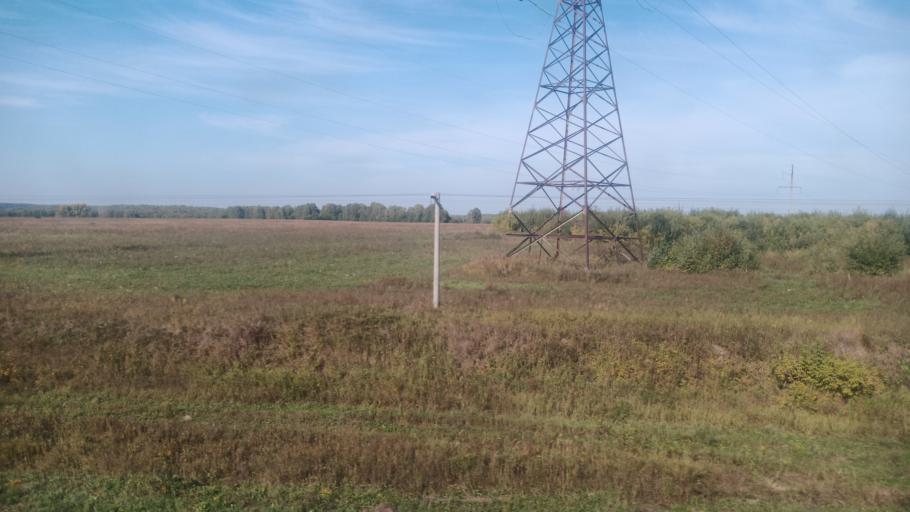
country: RU
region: Altai Krai
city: Troitskoye
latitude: 53.1000
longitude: 84.6750
